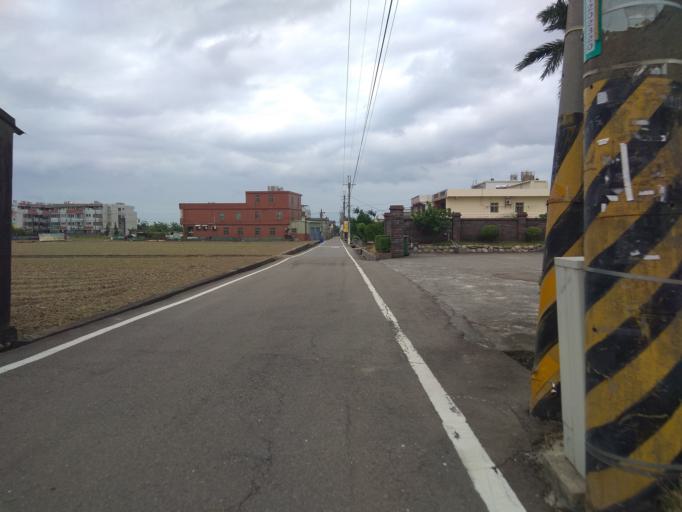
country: TW
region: Taiwan
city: Taoyuan City
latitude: 25.0498
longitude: 121.2200
